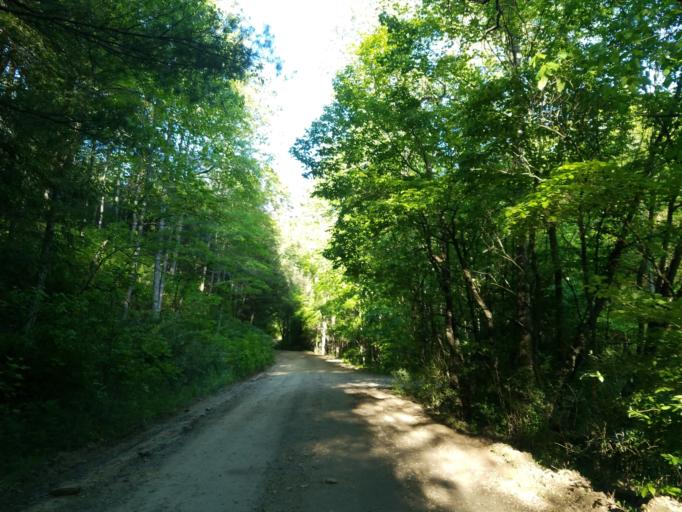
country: US
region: Georgia
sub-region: Lumpkin County
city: Dahlonega
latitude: 34.7010
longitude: -84.1482
